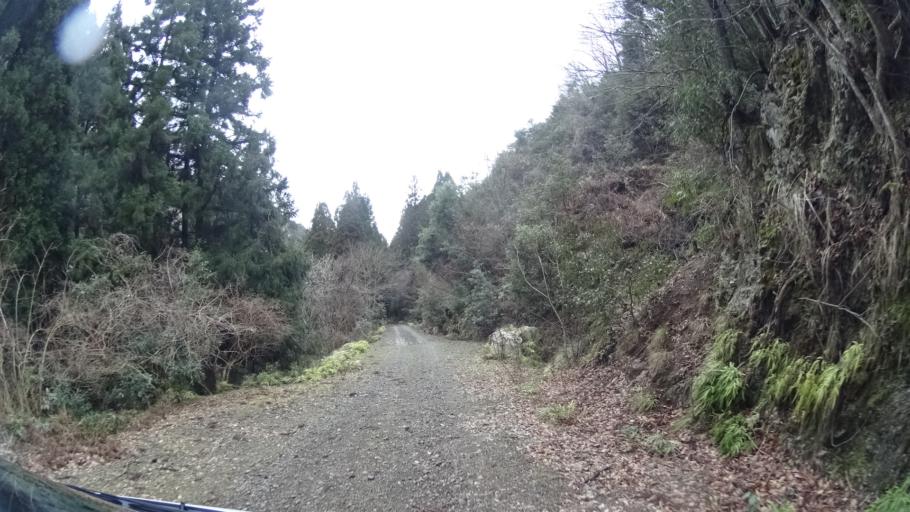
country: JP
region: Kyoto
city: Ayabe
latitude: 35.3116
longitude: 135.3747
